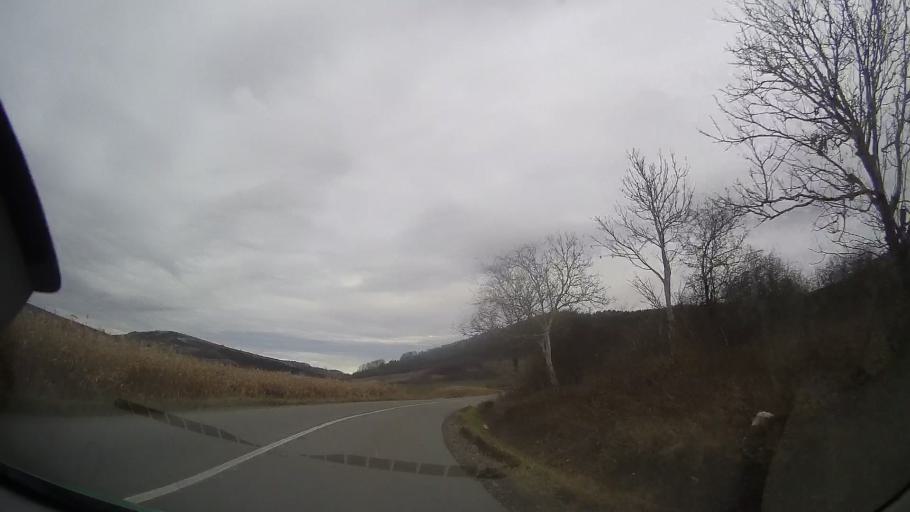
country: RO
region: Mures
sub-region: Comuna Bala
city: Bala
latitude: 46.7208
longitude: 24.5481
